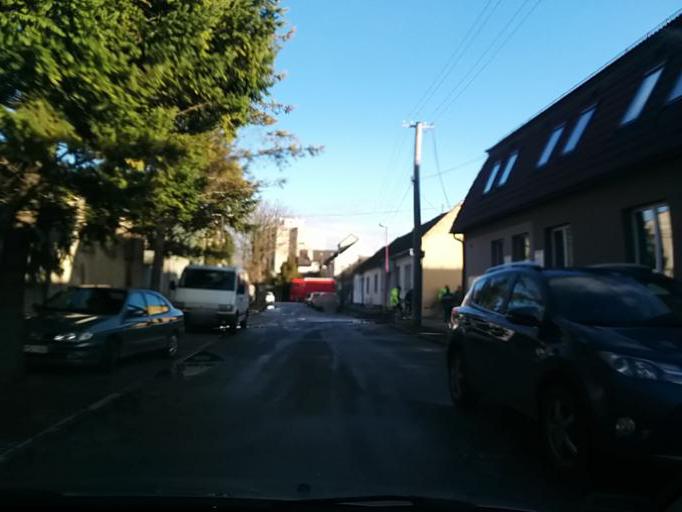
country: SK
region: Trenciansky
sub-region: Okres Nove Mesto nad Vahom
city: Nove Mesto nad Vahom
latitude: 48.7584
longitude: 17.8353
